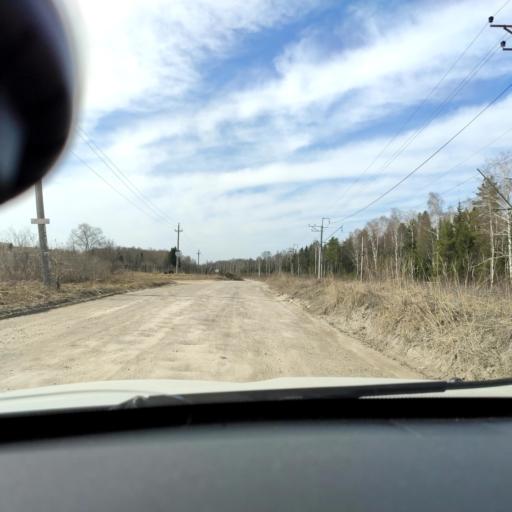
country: RU
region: Perm
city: Overyata
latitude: 58.0574
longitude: 55.9921
